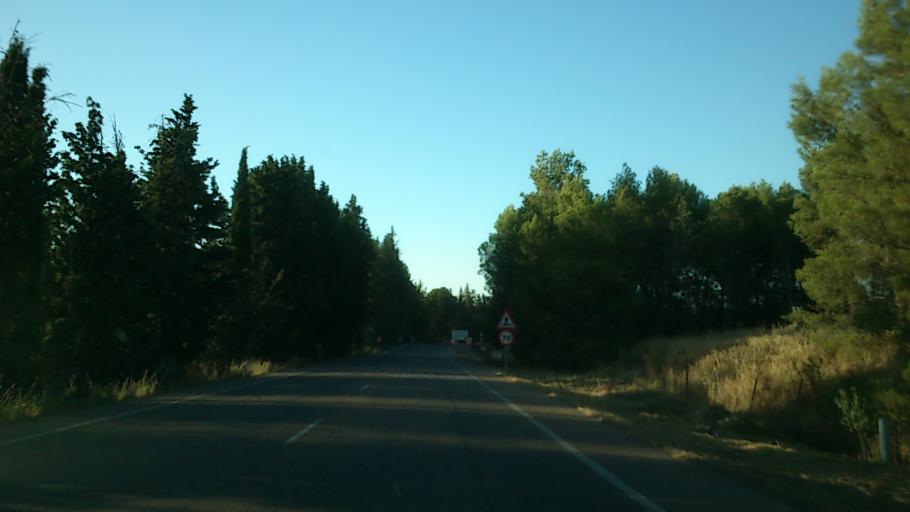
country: ES
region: Aragon
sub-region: Provincia de Zaragoza
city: Villanueva de Gallego
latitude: 41.7213
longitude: -0.8104
